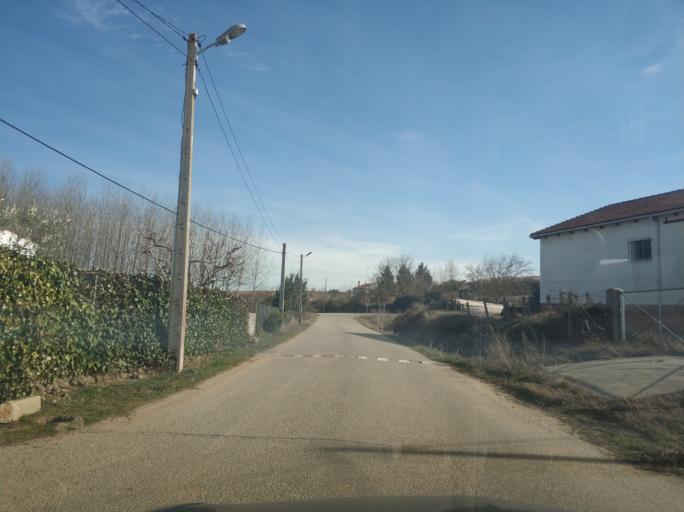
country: ES
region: Castille and Leon
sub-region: Provincia de Salamanca
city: Valverdon
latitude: 41.0390
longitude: -5.7891
